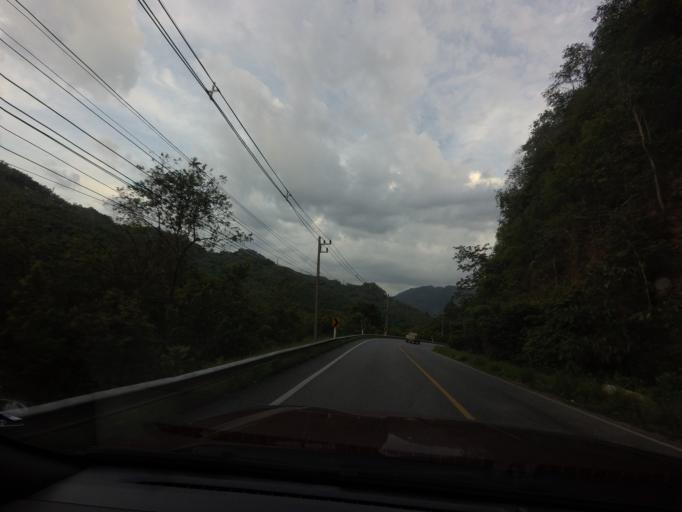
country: TH
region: Yala
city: Than To
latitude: 6.0151
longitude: 101.2006
